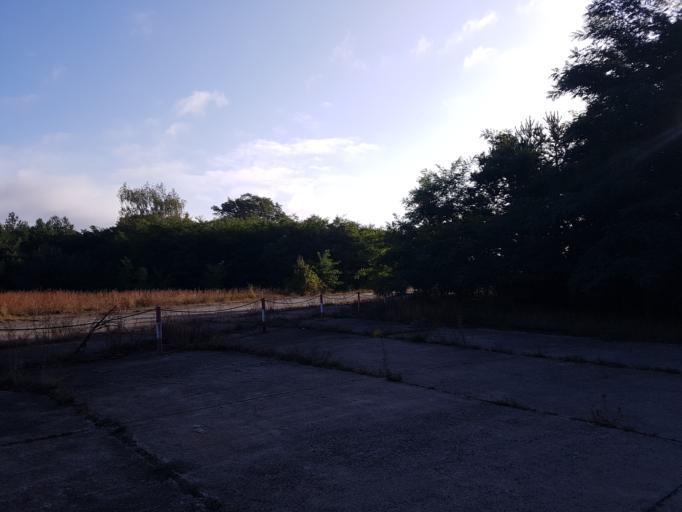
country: DE
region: Brandenburg
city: Finsterwalde
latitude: 51.6049
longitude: 13.7516
